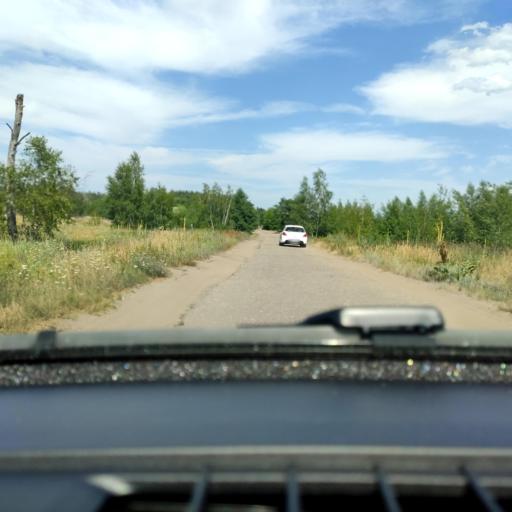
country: RU
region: Voronezj
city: Somovo
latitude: 51.7710
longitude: 39.3366
